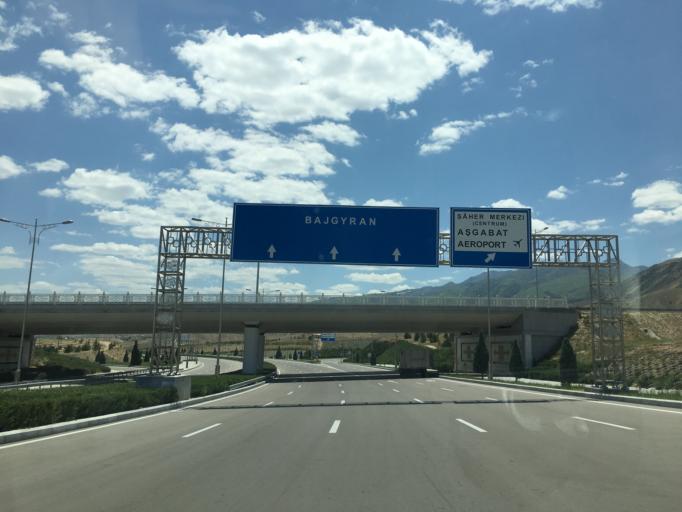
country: TM
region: Ahal
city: Ashgabat
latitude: 37.8896
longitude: 58.2523
